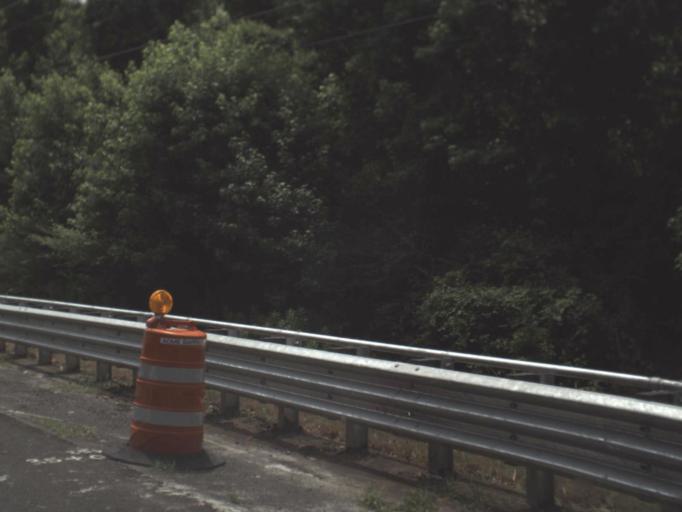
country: US
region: Florida
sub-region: Nassau County
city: Nassau Village-Ratliff
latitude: 30.4377
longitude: -81.7548
